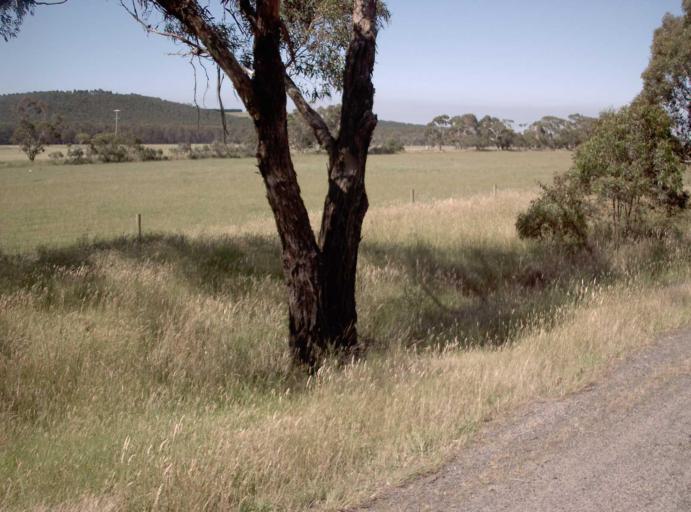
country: AU
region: Victoria
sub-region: Latrobe
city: Morwell
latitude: -38.6331
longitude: 146.5478
